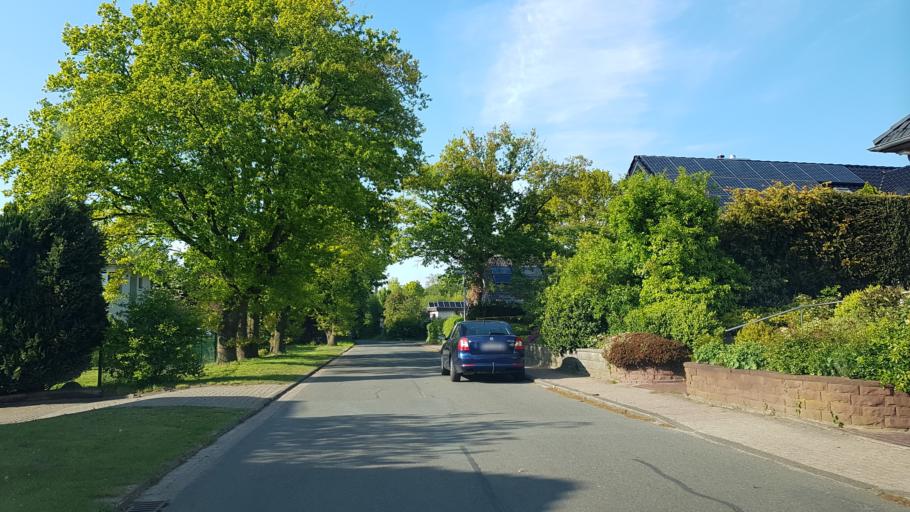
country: DE
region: Lower Saxony
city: Langen
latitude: 53.6156
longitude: 8.5925
